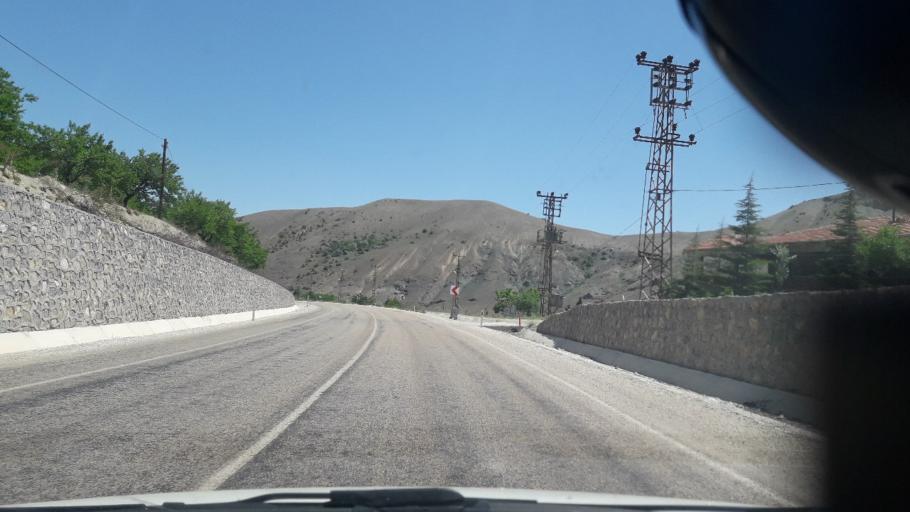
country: TR
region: Malatya
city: Hekimhan
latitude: 38.8296
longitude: 37.8527
